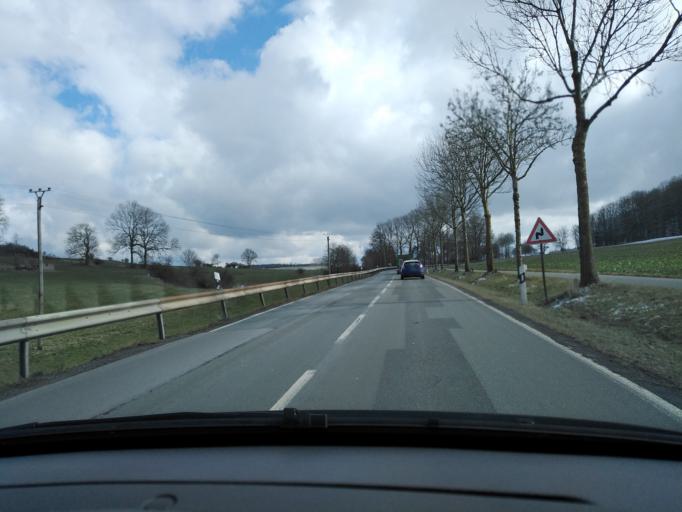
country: DE
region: North Rhine-Westphalia
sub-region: Regierungsbezirk Arnsberg
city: Brilon
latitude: 51.4050
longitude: 8.6213
